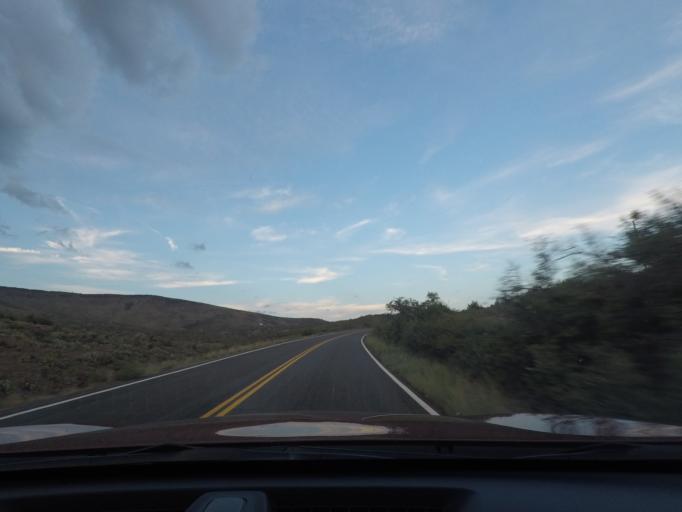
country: US
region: Arizona
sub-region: Yavapai County
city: Congress
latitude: 34.4701
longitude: -112.8080
